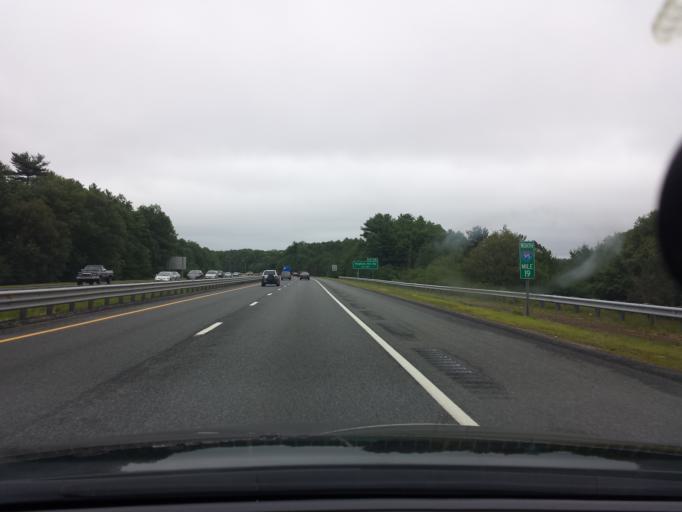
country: US
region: Rhode Island
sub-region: Kent County
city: West Greenwich
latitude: 41.6497
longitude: -71.5922
